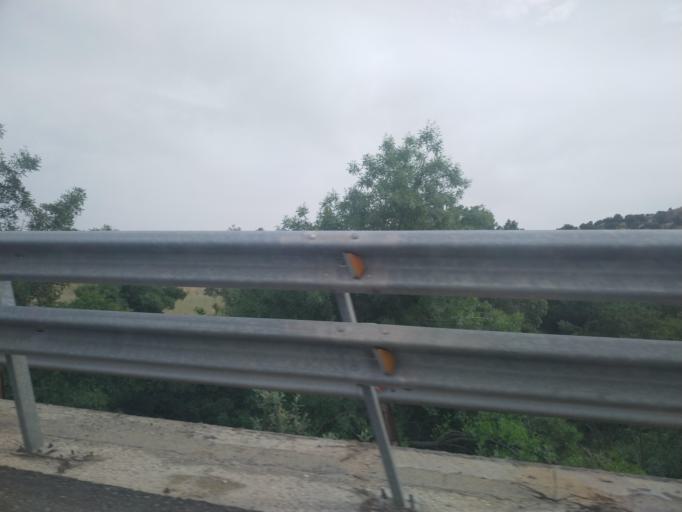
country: ES
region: Castille-La Mancha
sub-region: Province of Toledo
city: Layos
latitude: 39.8154
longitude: -4.0975
